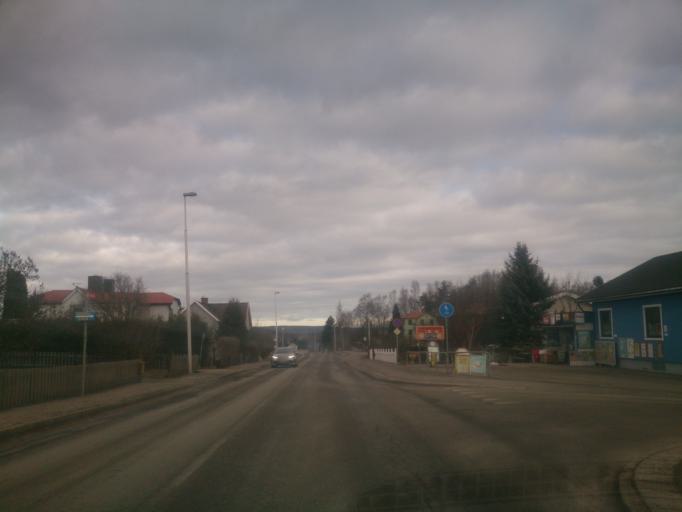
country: SE
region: OEstergoetland
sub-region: Motala Kommun
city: Motala
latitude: 58.5272
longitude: 15.0549
